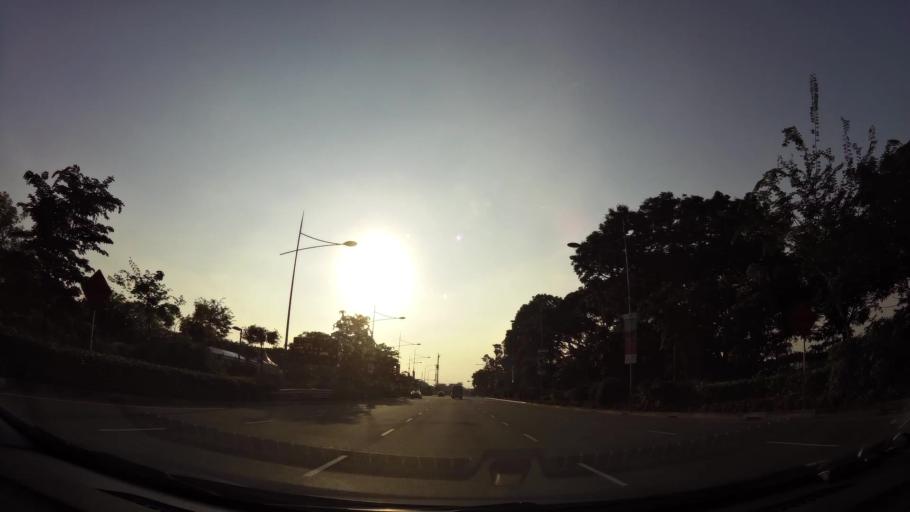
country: SG
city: Singapore
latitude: 1.2764
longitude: 103.8609
